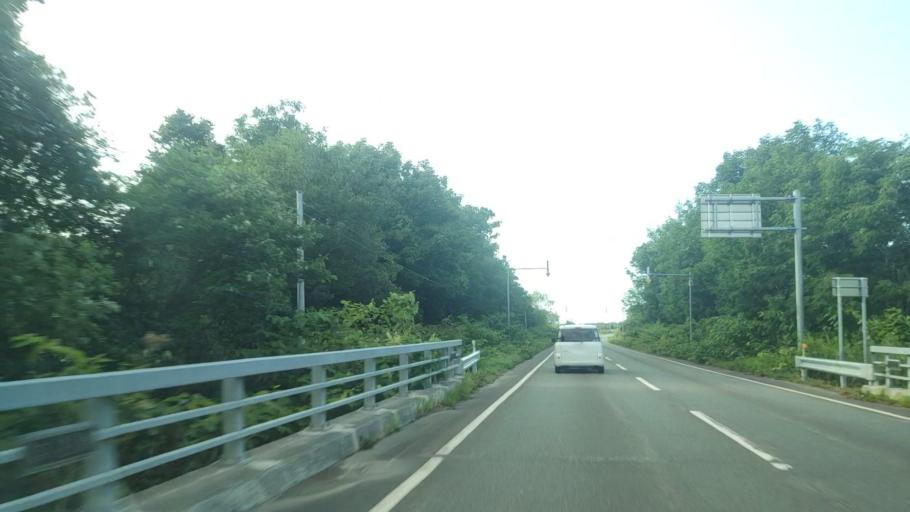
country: JP
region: Hokkaido
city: Makubetsu
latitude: 45.0525
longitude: 141.7502
